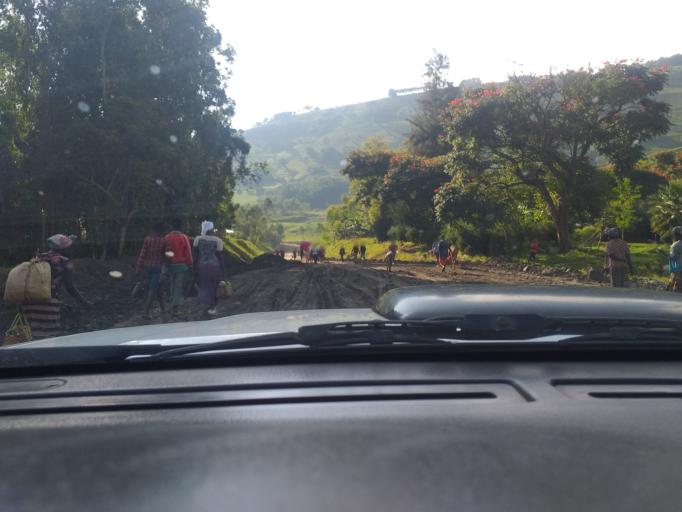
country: ET
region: Southern Nations, Nationalities, and People's Region
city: Bako
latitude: 5.9793
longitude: 36.5700
